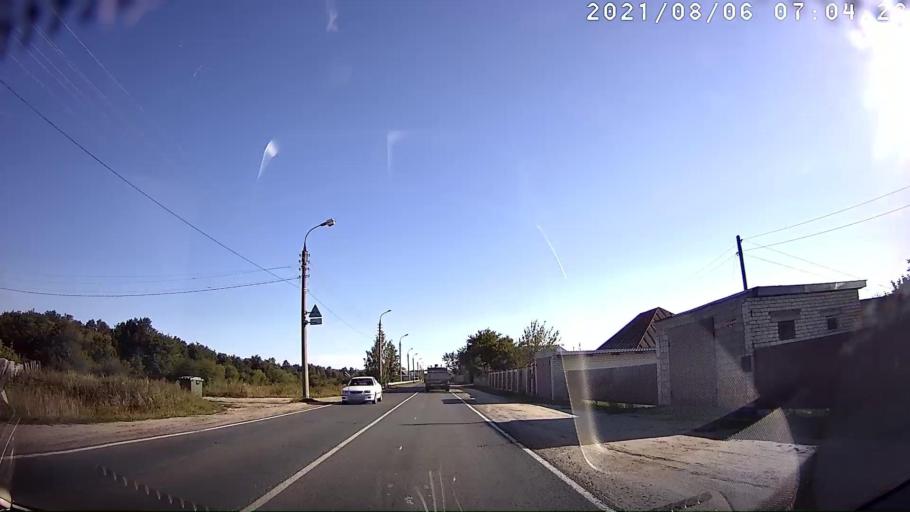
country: RU
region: Mariy-El
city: Yoshkar-Ola
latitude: 56.5472
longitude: 47.9823
